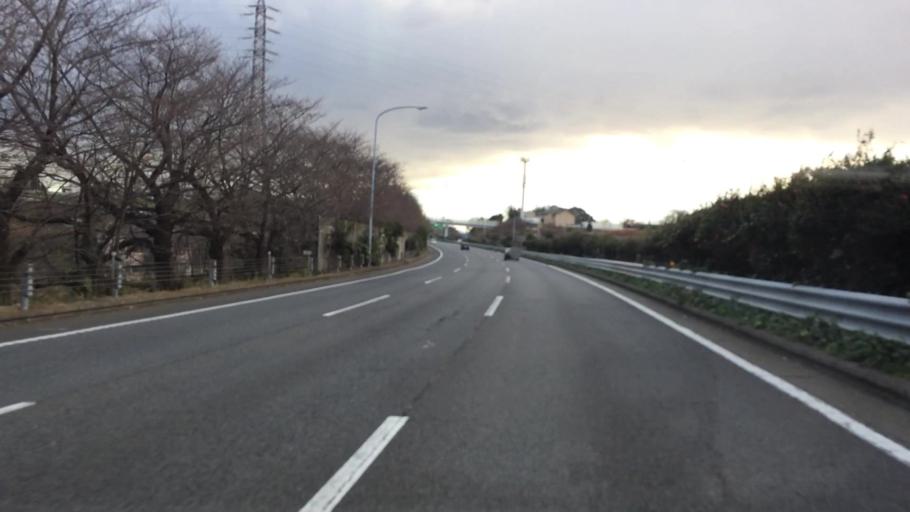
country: JP
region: Kanagawa
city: Yokohama
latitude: 35.4978
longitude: 139.5914
